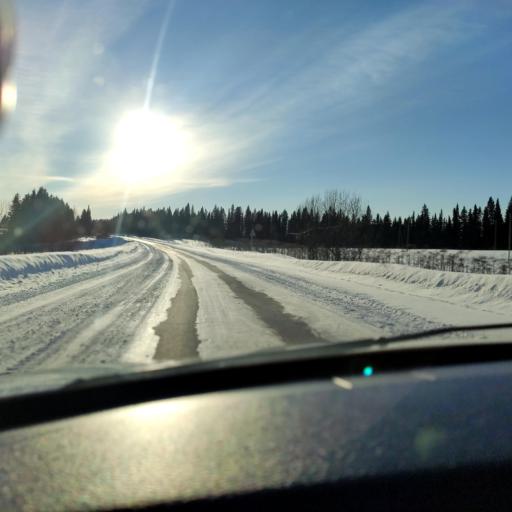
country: RU
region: Perm
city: Polazna
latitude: 58.3434
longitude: 56.4470
